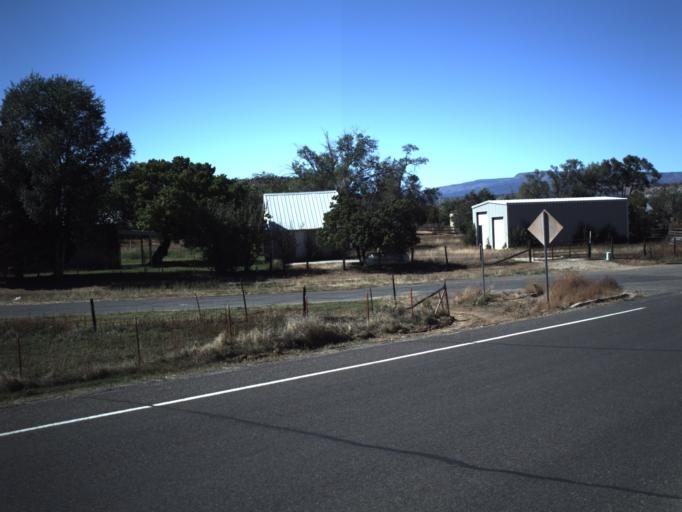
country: US
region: Utah
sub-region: Wayne County
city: Loa
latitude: 37.7690
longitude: -111.5940
